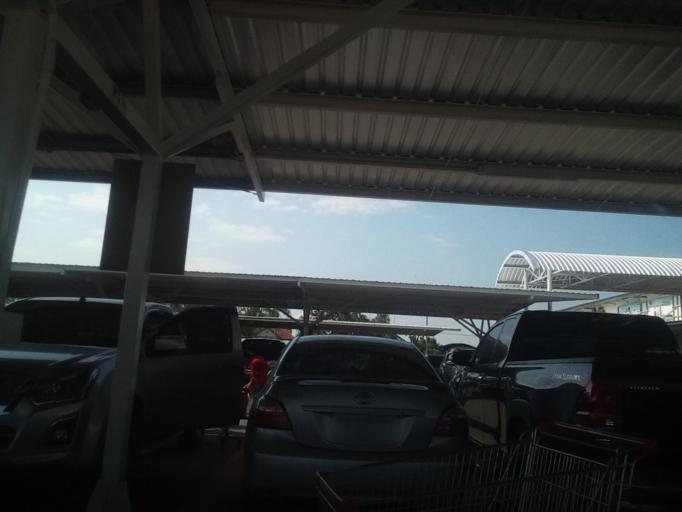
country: TH
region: Lamphun
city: Lamphun
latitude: 18.5938
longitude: 99.0416
